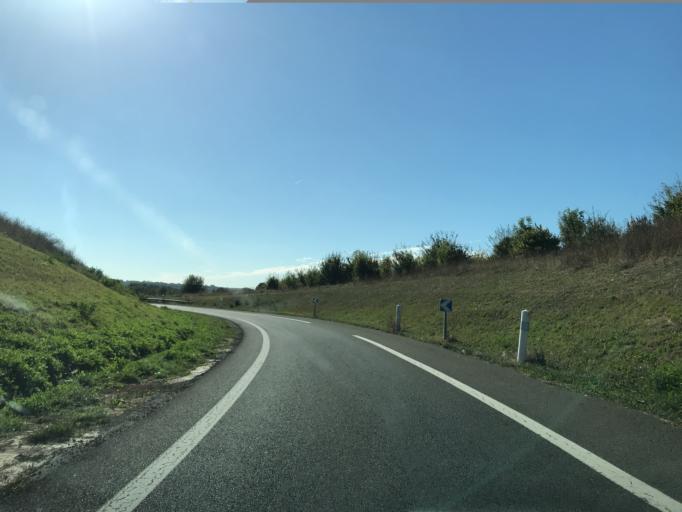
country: FR
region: Ile-de-France
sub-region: Departement de Seine-et-Marne
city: Bouleurs
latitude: 48.8859
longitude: 2.8918
